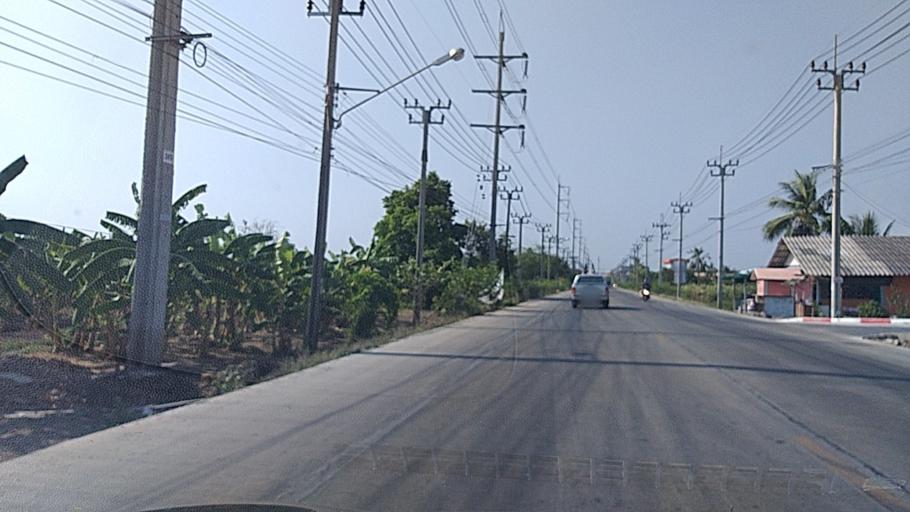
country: TH
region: Nonthaburi
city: Bang Yai
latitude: 13.9032
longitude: 100.3243
